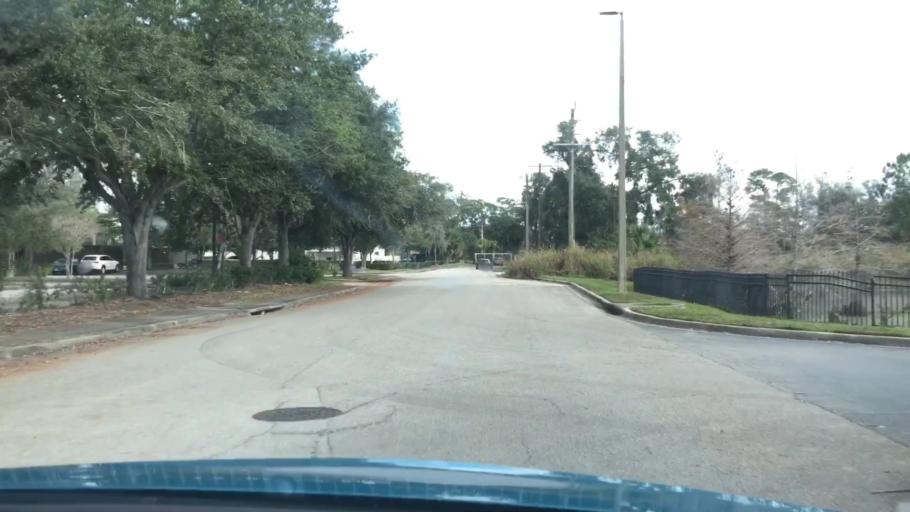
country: US
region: Florida
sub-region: Seminole County
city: Lake Mary
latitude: 28.8104
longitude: -81.3337
